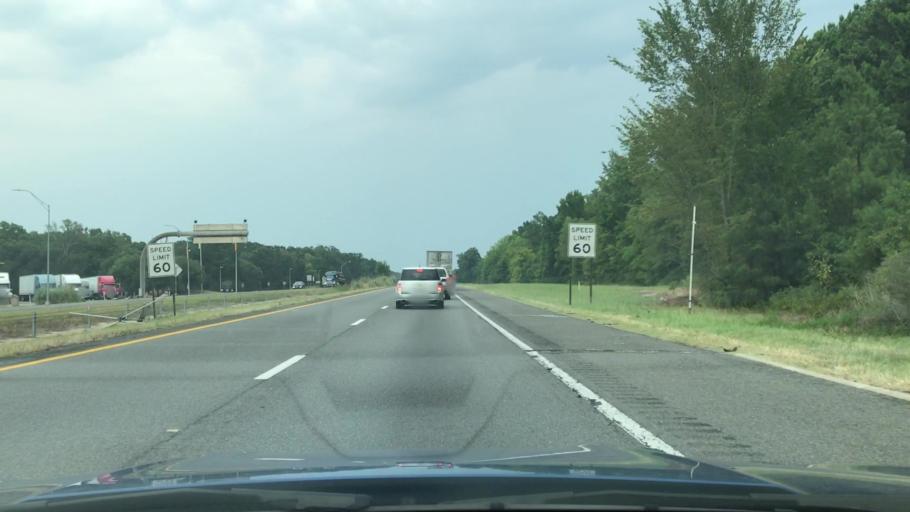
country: US
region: Texas
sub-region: Harrison County
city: Waskom
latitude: 32.4631
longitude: -94.0471
